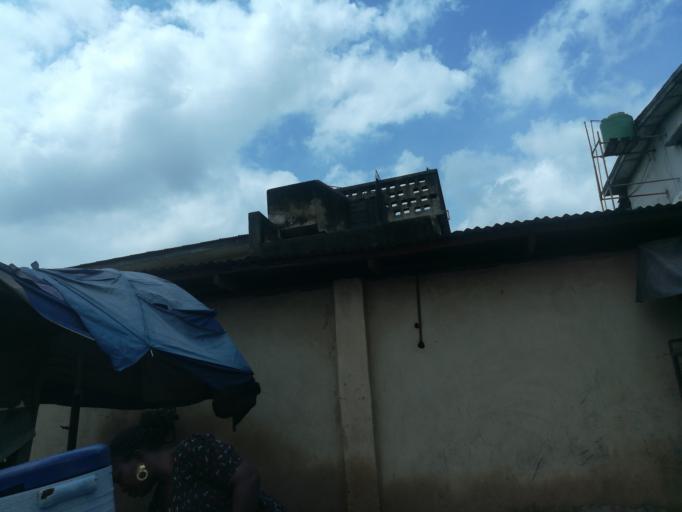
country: NG
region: Lagos
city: Somolu
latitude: 6.5349
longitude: 3.3643
